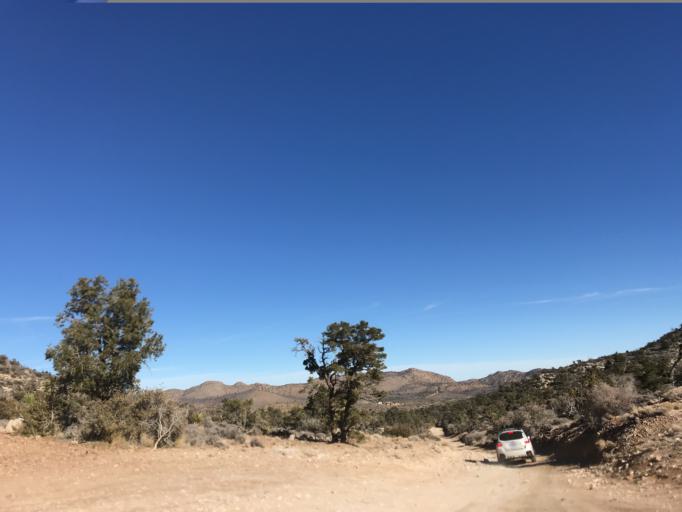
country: US
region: California
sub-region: San Bernardino County
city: Big Bear City
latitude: 34.2314
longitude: -116.6582
